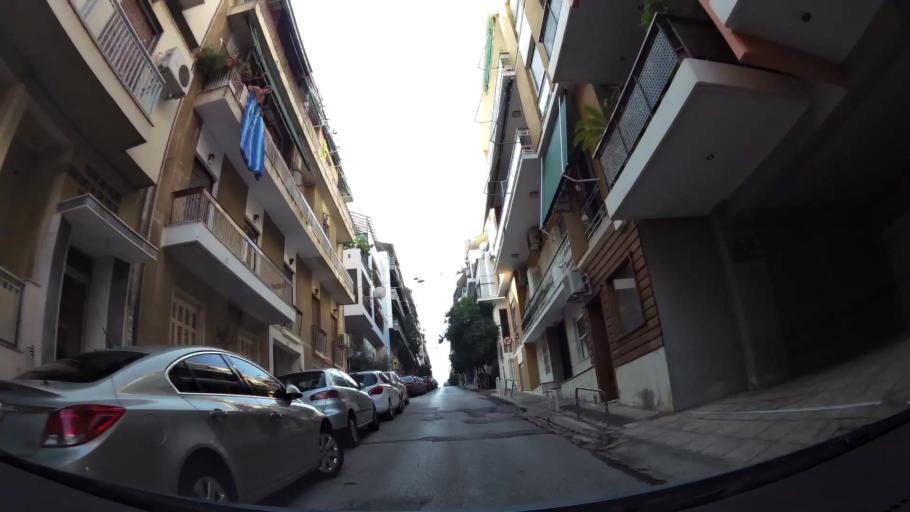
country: GR
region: Attica
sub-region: Nomarchia Athinas
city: Kaisariani
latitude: 37.9770
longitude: 23.7690
